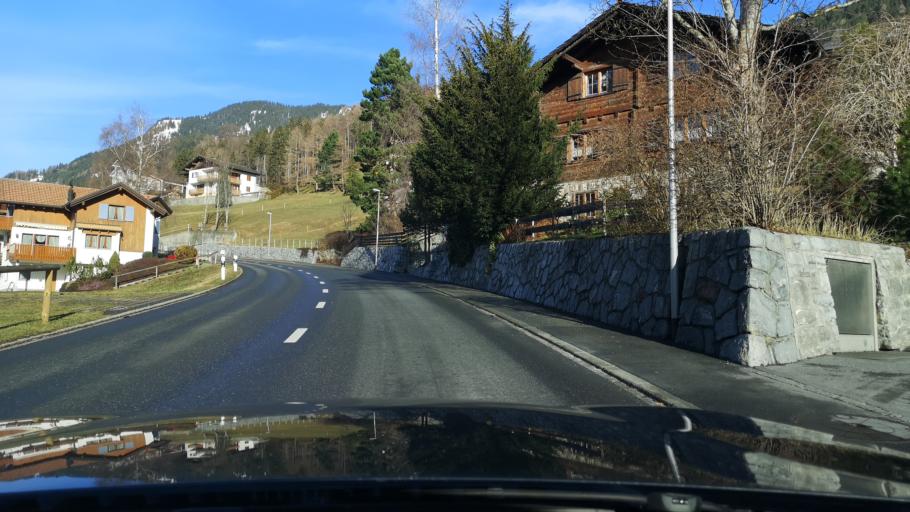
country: LI
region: Triesenberg
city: Triesenberg
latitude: 47.1140
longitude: 9.5502
